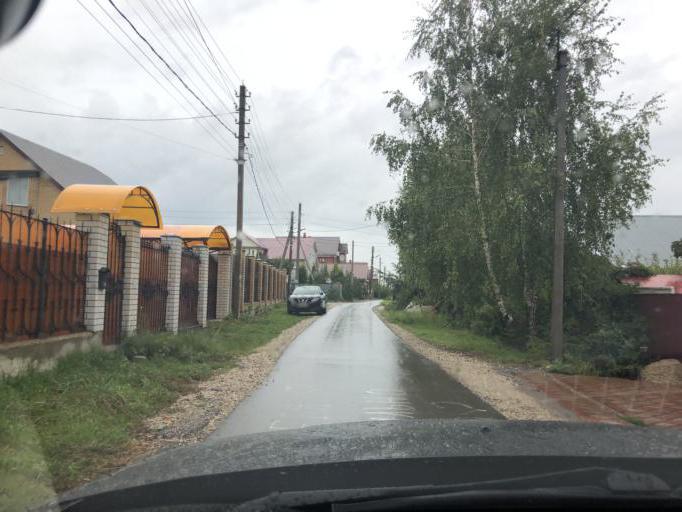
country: RU
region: Tula
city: Barsuki
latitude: 54.1999
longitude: 37.5186
